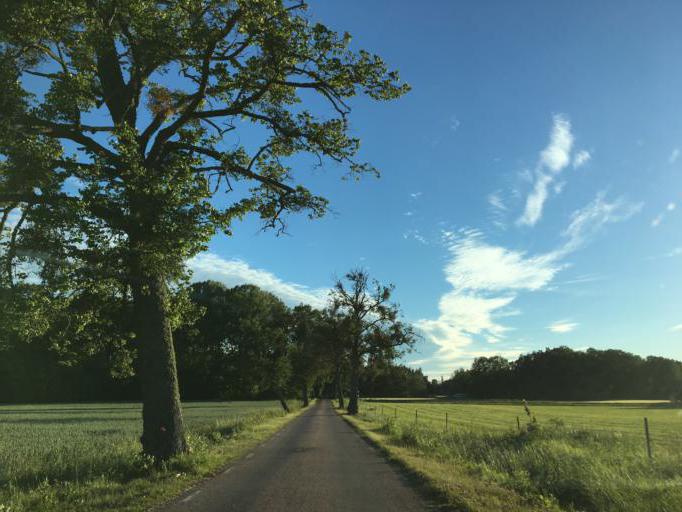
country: SE
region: Vaestmanland
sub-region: Vasteras
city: Vasteras
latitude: 59.5490
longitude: 16.5414
